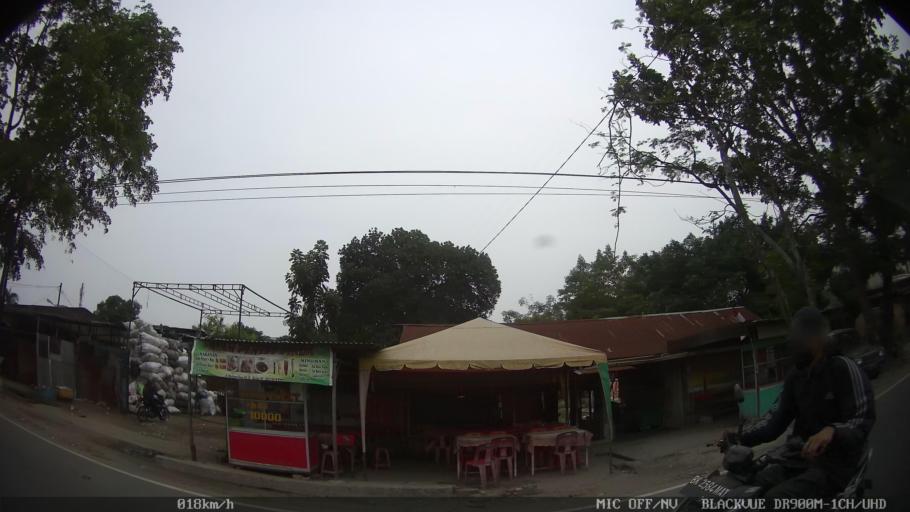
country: ID
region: North Sumatra
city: Medan
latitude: 3.5680
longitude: 98.7226
